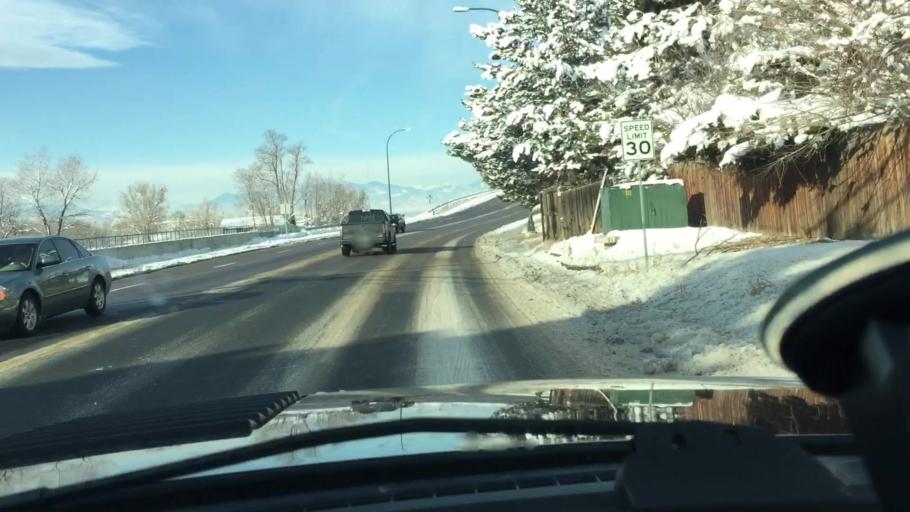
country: US
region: Colorado
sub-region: Adams County
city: Westminster
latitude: 39.8419
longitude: -105.0357
